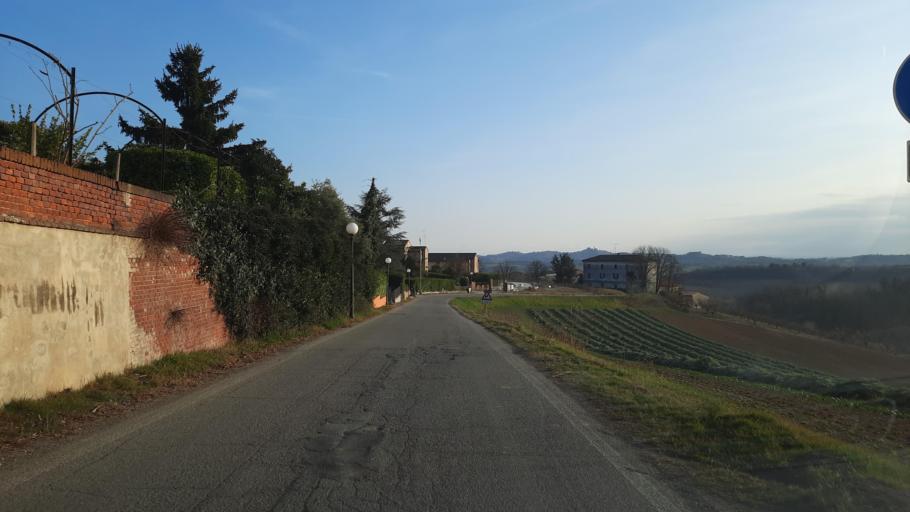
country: IT
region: Piedmont
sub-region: Provincia di Alessandria
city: Cella Monte
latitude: 45.0725
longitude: 8.3929
